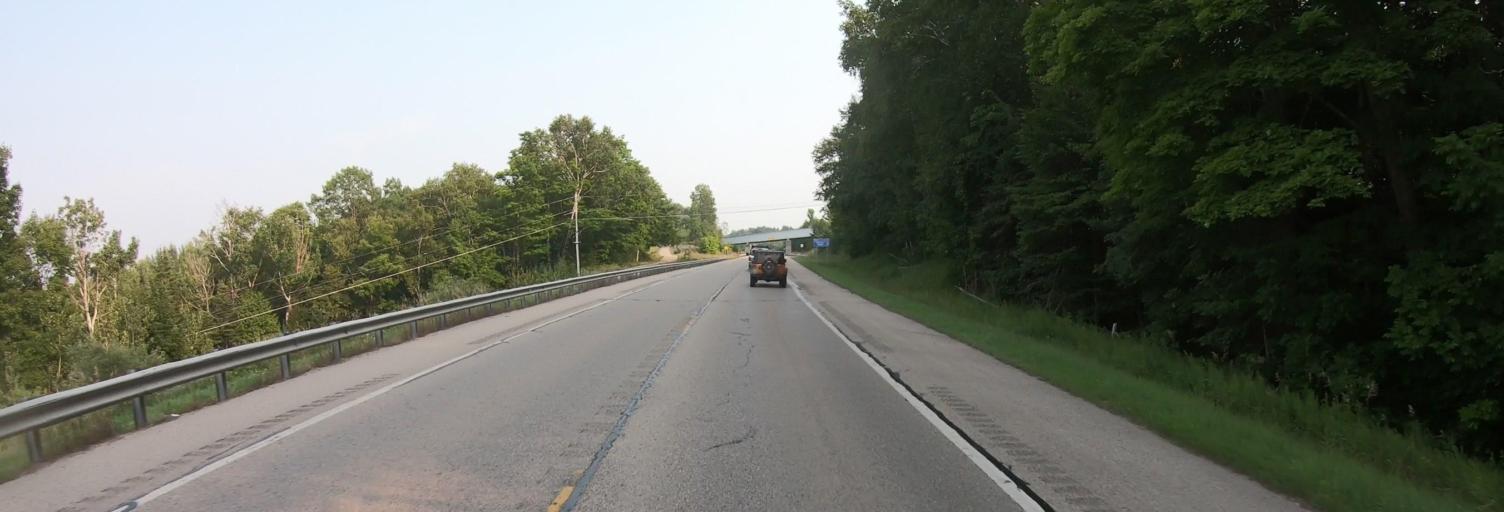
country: US
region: Michigan
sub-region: Emmet County
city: Harbor Springs
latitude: 45.3652
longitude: -85.1210
